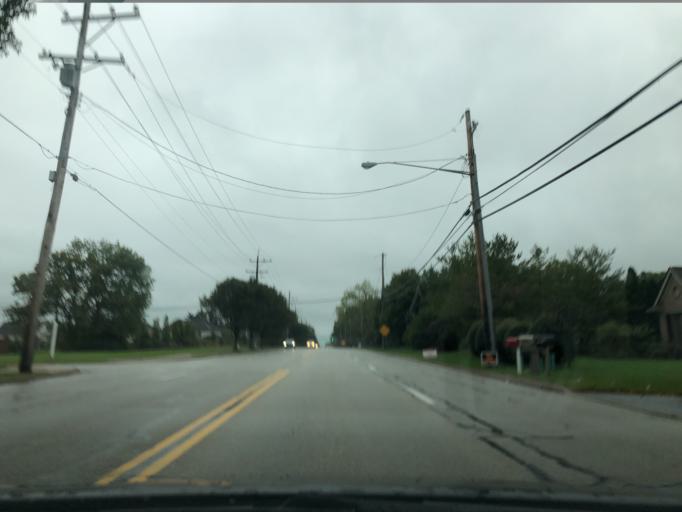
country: US
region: Ohio
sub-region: Hamilton County
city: Rossmoyne
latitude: 39.2174
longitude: -84.3785
